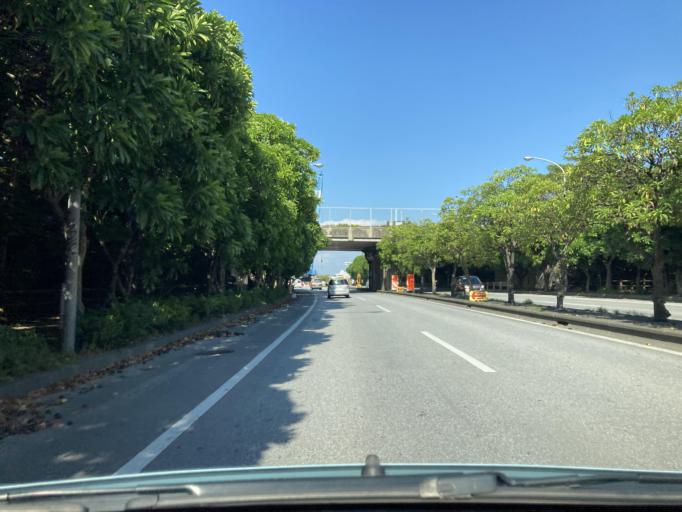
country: JP
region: Okinawa
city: Okinawa
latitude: 26.3089
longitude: 127.8266
